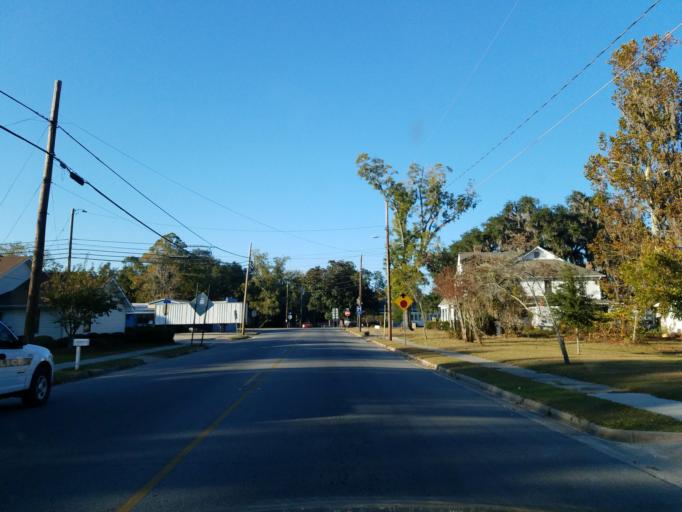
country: US
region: Georgia
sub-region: Lanier County
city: Lakeland
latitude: 31.0407
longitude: -83.0713
